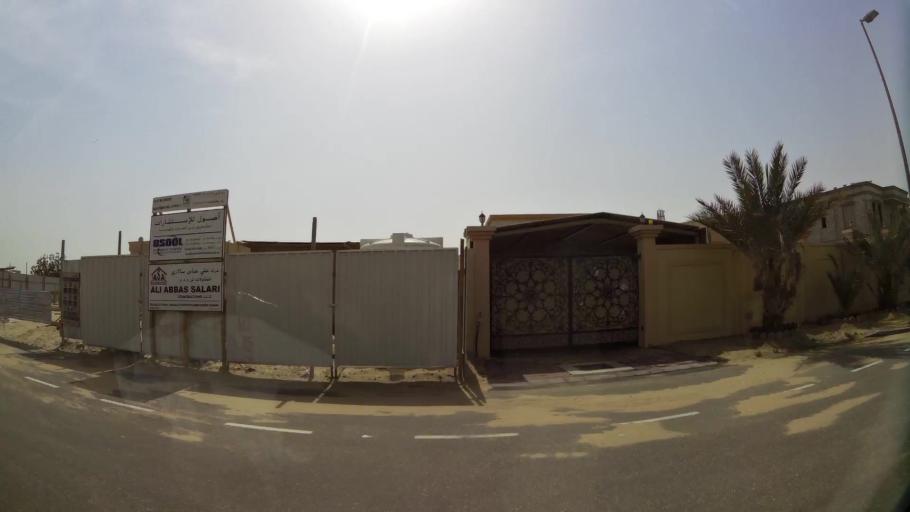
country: AE
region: Ash Shariqah
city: Sharjah
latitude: 25.2580
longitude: 55.4691
